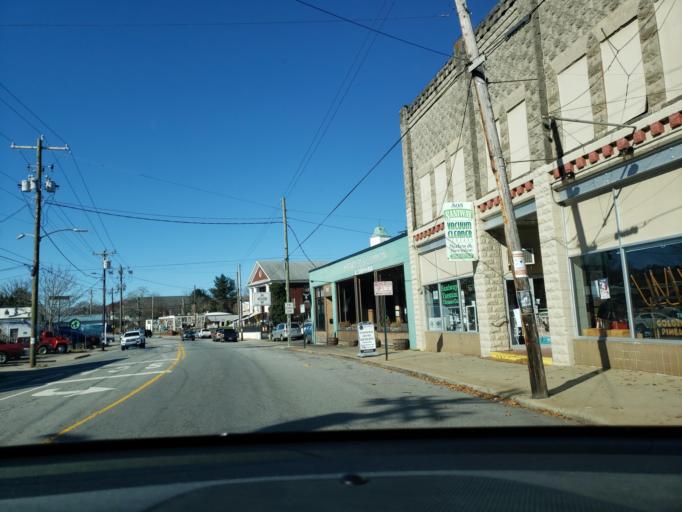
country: US
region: North Carolina
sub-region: Buncombe County
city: Asheville
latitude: 35.5784
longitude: -82.5838
